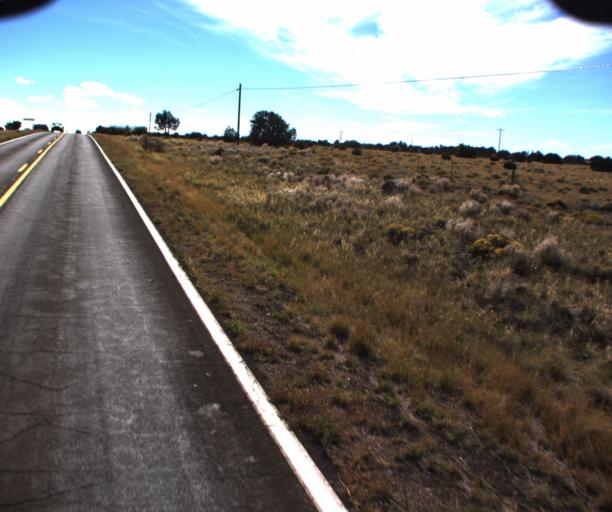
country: US
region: Arizona
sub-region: Apache County
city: Saint Johns
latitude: 34.4197
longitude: -109.6429
